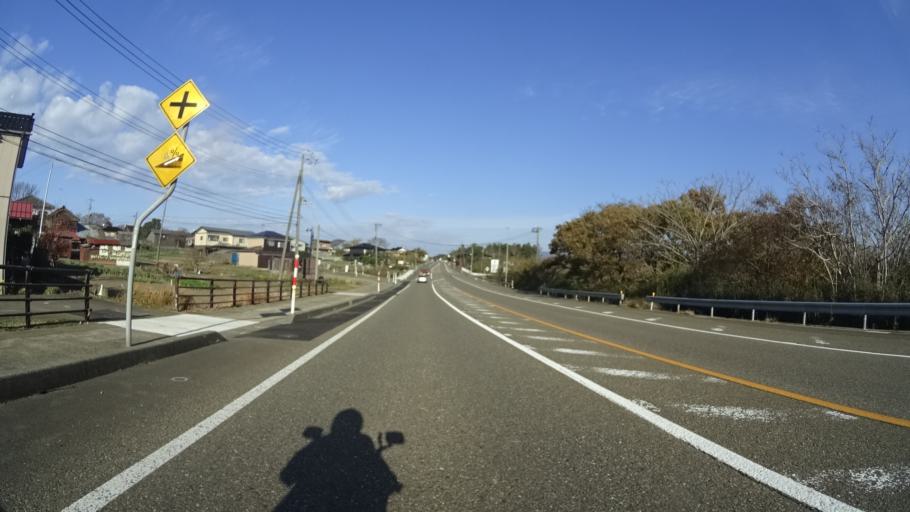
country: JP
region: Niigata
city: Joetsu
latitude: 37.2480
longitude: 138.3547
